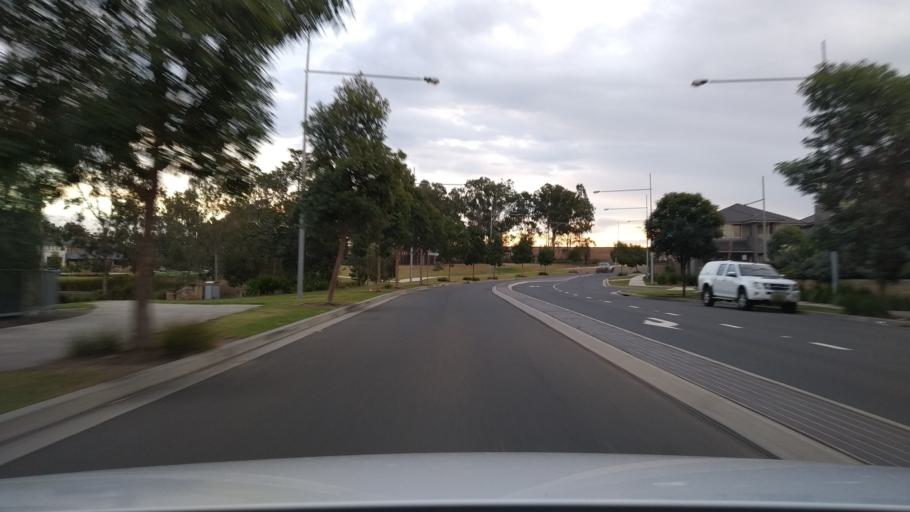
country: AU
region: New South Wales
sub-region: Camden
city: Narellan
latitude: -34.0082
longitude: 150.7388
